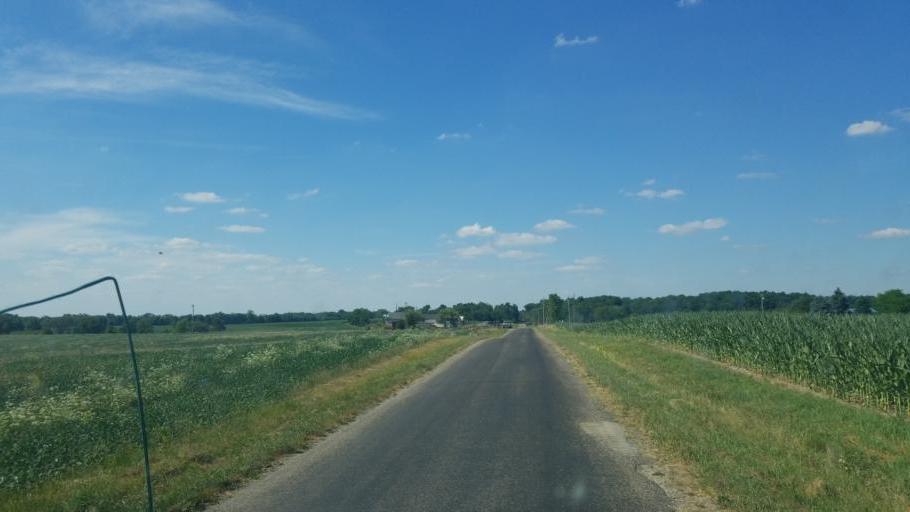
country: US
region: Ohio
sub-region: Williams County
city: Edgerton
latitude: 41.3802
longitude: -84.7863
